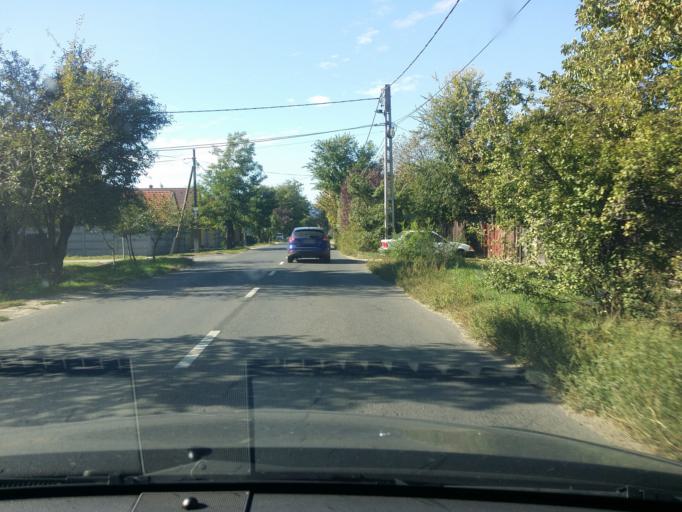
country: HU
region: Pest
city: God
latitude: 47.6833
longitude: 19.1695
